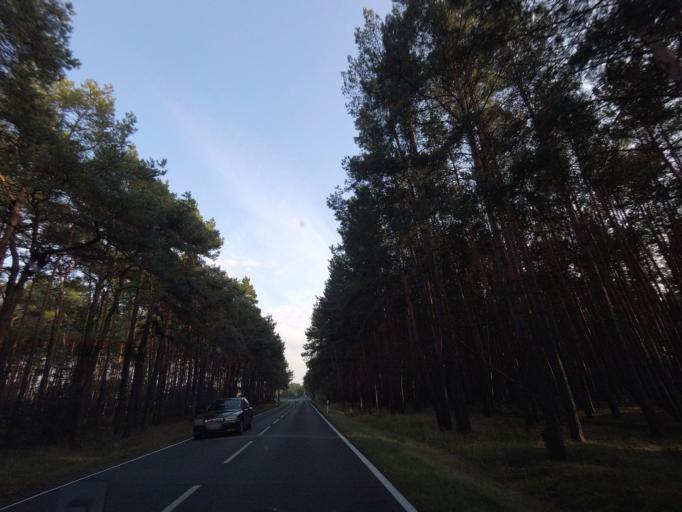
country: DE
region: Brandenburg
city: Bruck
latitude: 52.1707
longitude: 12.7654
